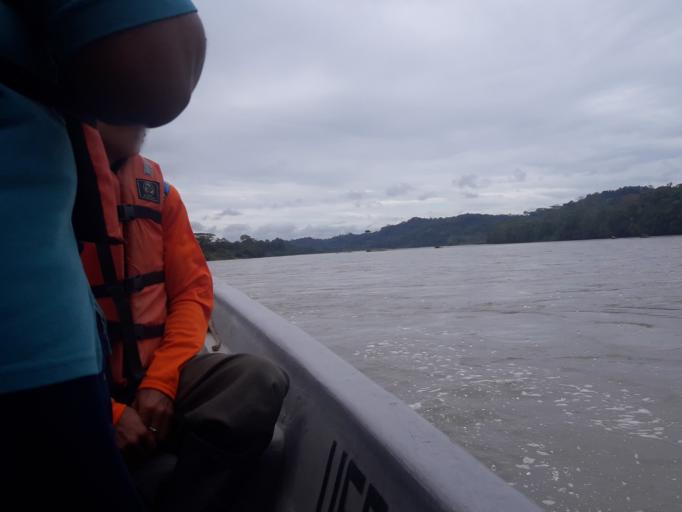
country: EC
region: Orellana
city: Boca Suno
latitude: -0.8805
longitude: -77.2933
